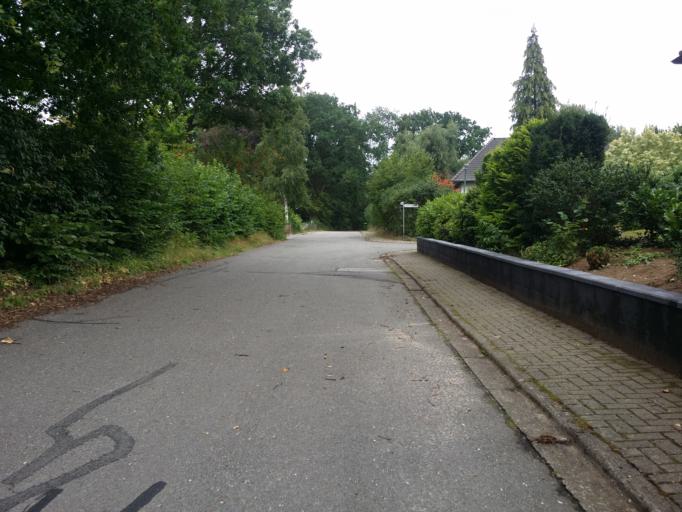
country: DE
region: Schleswig-Holstein
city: Oldendorf
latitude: 53.9469
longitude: 9.4596
